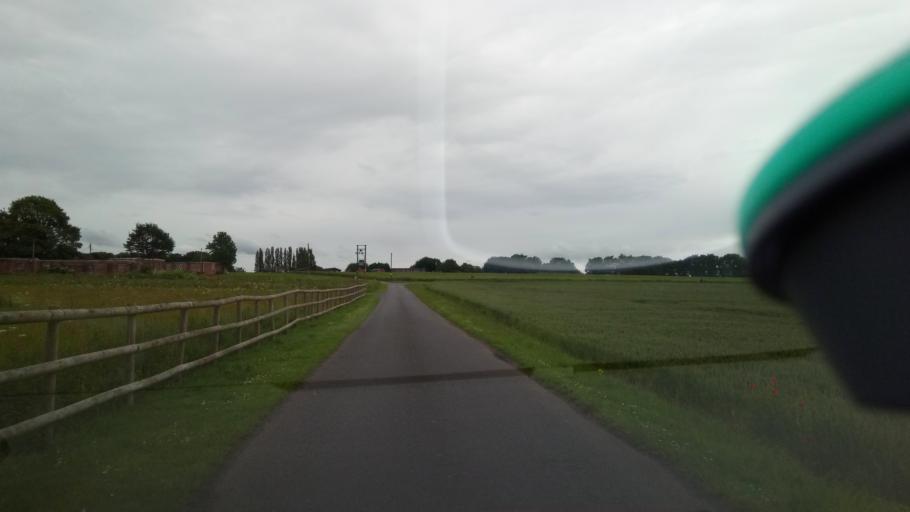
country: GB
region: England
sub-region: Derbyshire
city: Melbourne
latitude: 52.8472
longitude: -1.4163
